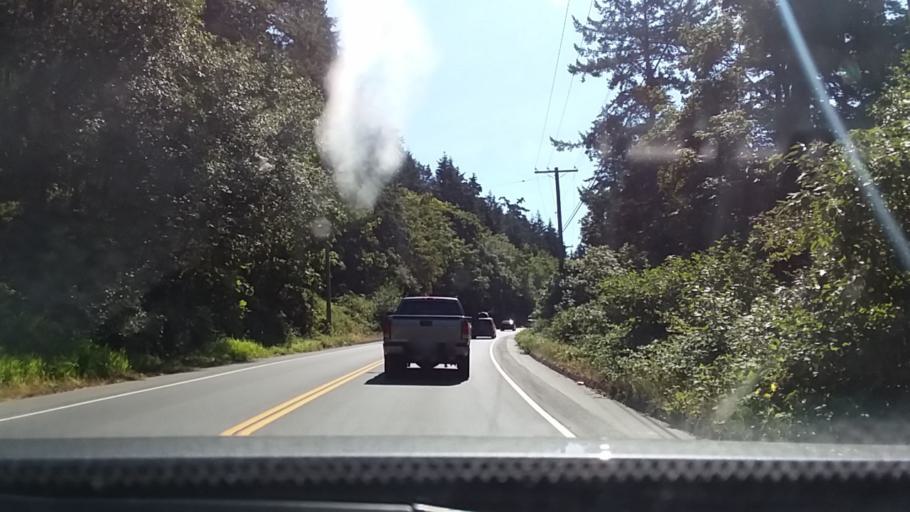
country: CA
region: British Columbia
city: Courtenay
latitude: 49.6775
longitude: -124.9535
